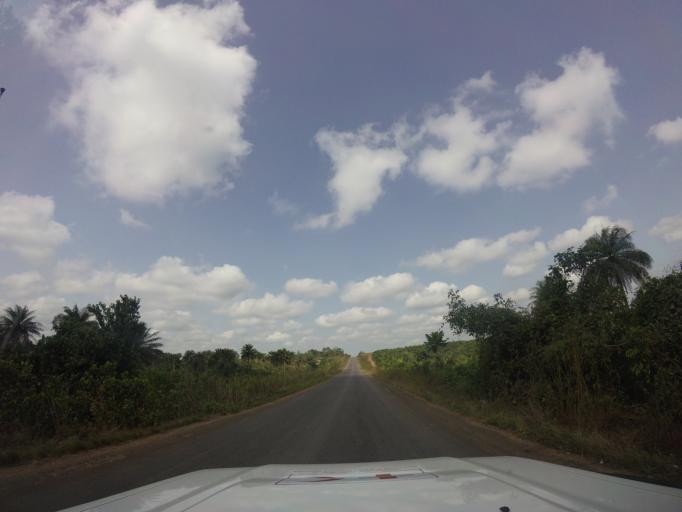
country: LR
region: Bomi
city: Tubmanburg
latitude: 6.7316
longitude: -11.0001
